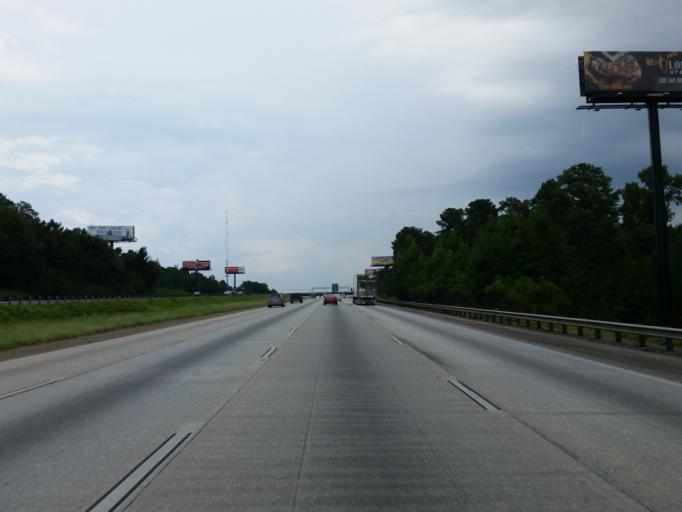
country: US
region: Georgia
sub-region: Monroe County
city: Forsyth
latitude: 32.9672
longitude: -83.8220
